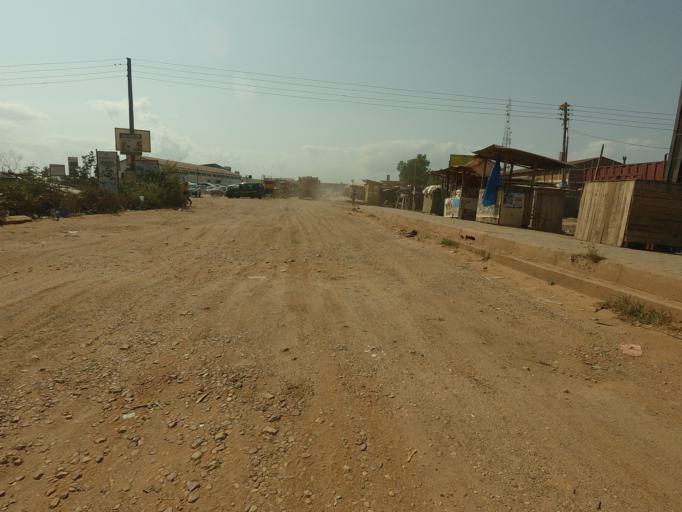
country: GH
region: Greater Accra
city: Medina Estates
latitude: 5.6358
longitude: -0.1257
